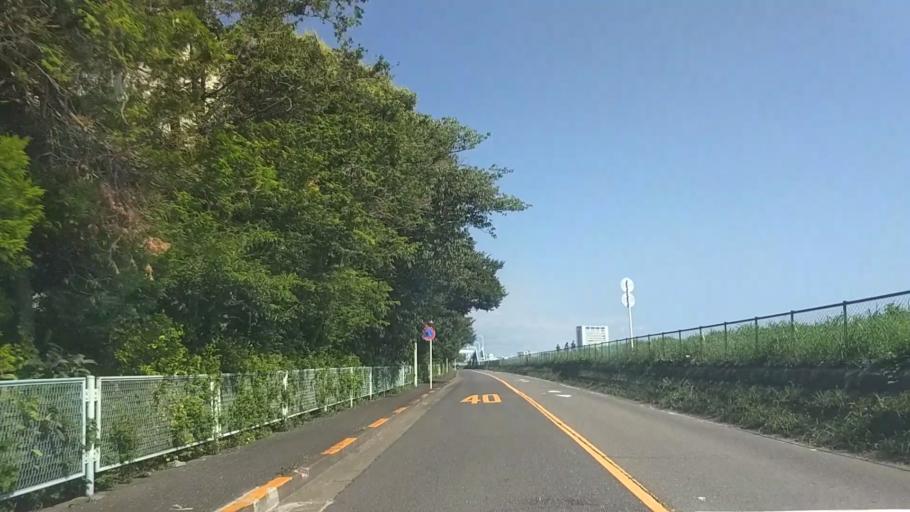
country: JP
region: Kanagawa
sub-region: Kawasaki-shi
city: Kawasaki
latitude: 35.5607
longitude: 139.6866
